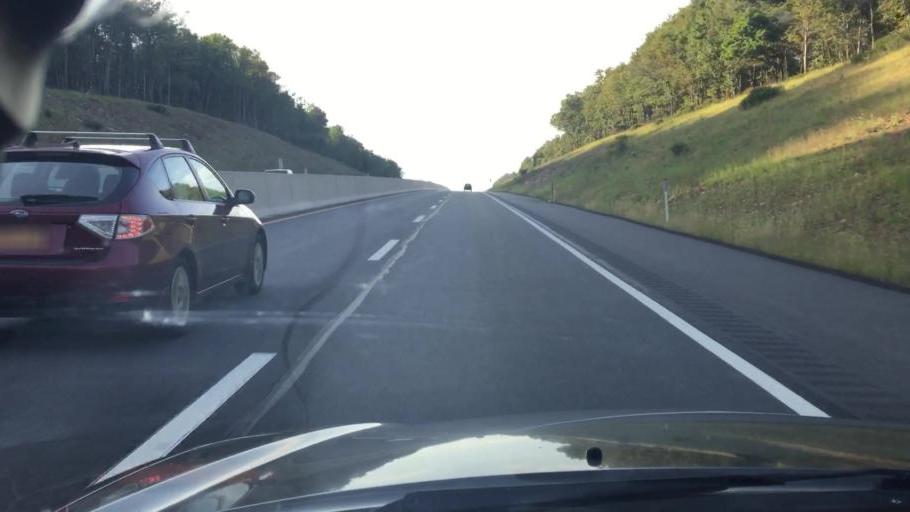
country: US
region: Pennsylvania
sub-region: Carbon County
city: Towamensing Trails
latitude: 41.0308
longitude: -75.6540
